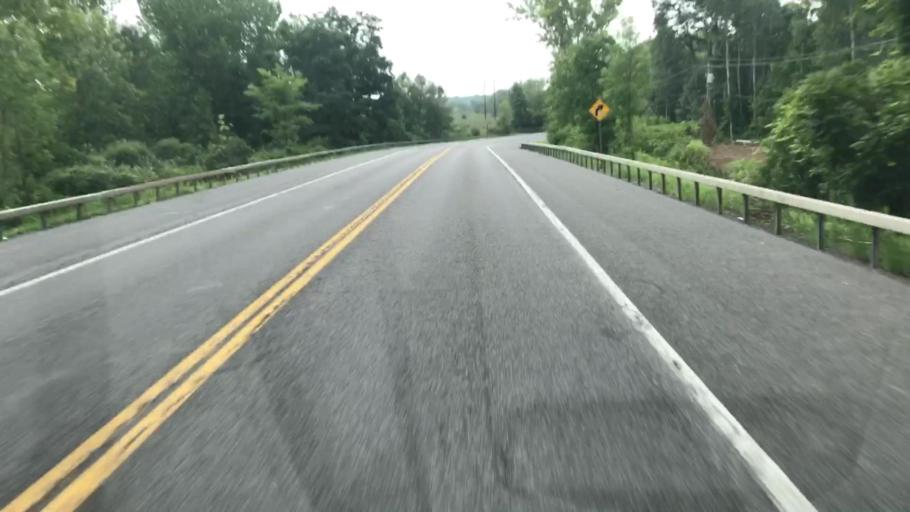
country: US
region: New York
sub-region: Onondaga County
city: Liverpool
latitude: 43.1706
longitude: -76.1975
